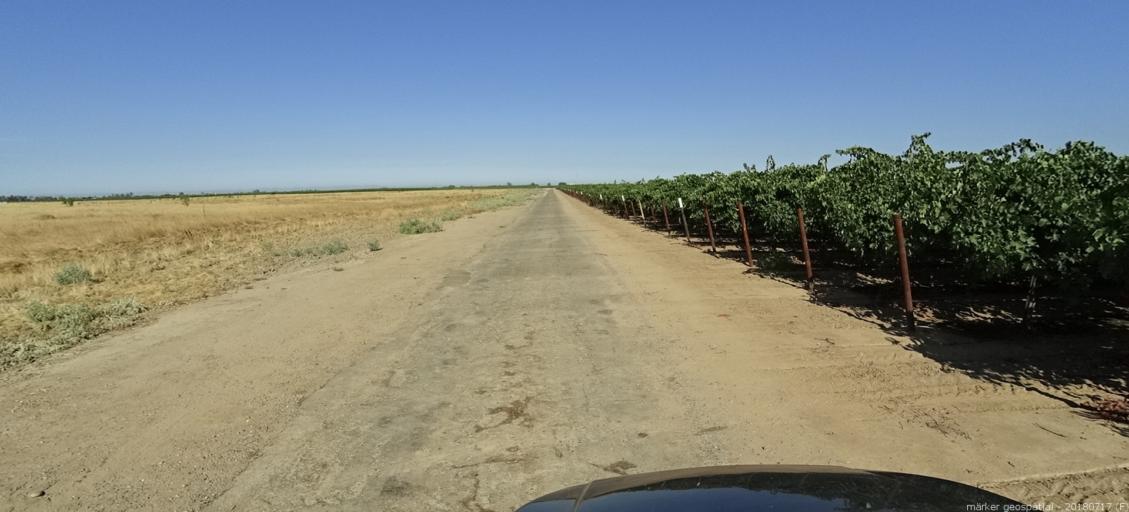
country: US
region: California
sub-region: Madera County
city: Madera Acres
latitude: 37.0399
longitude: -120.1185
